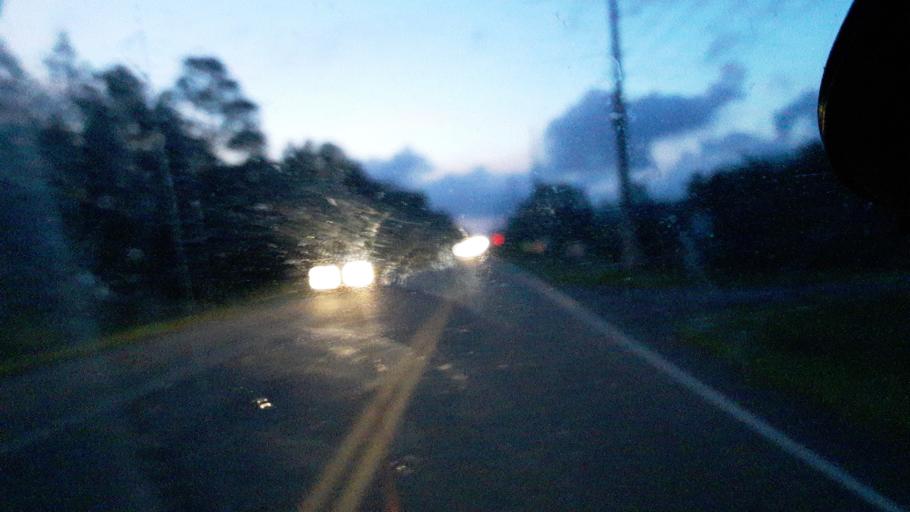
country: US
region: North Carolina
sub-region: Brunswick County
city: Oak Island
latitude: 33.9921
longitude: -78.2148
